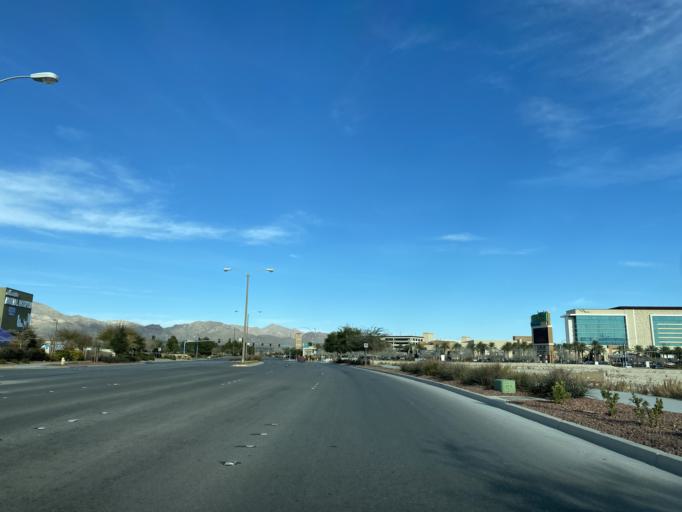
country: US
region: Nevada
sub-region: Clark County
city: North Las Vegas
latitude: 36.2914
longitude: -115.1853
